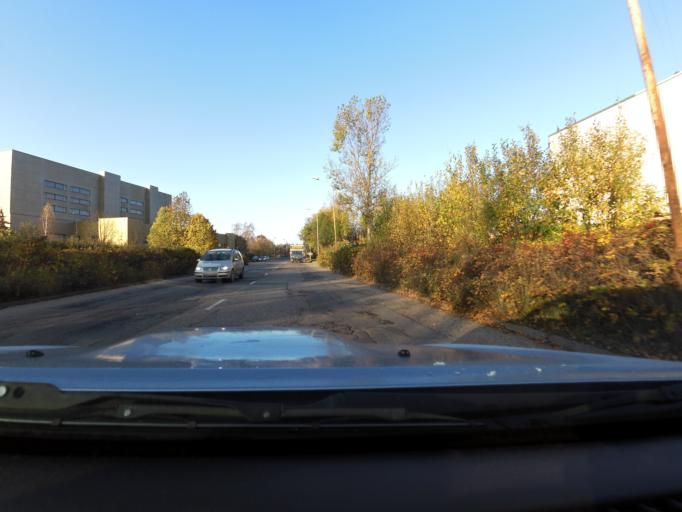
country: LT
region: Vilnius County
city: Vilkpede
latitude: 54.6372
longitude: 25.2597
